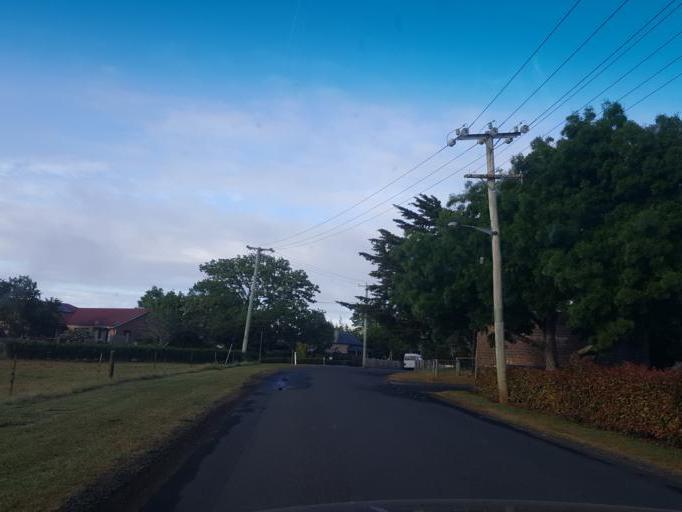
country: AU
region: Tasmania
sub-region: Northern Midlands
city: Evandale
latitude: -41.5659
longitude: 147.2532
